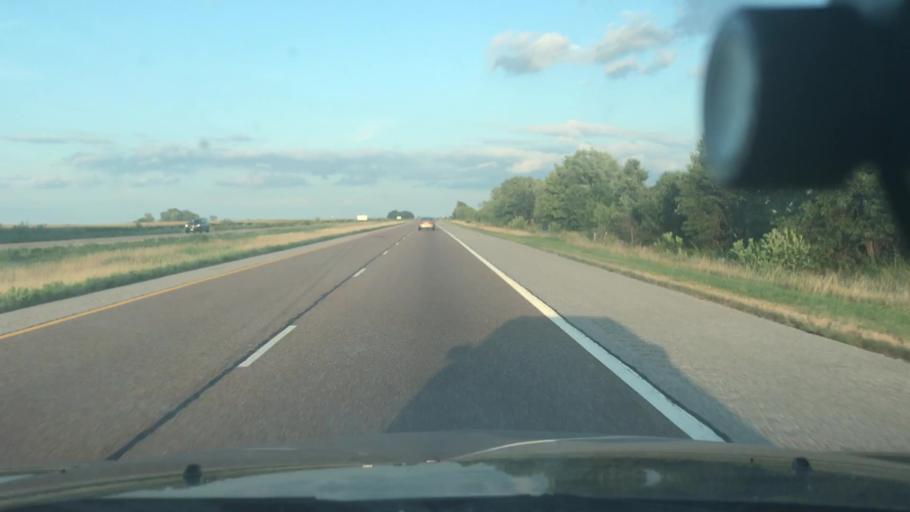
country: US
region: Illinois
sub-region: Clinton County
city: New Baden
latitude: 38.5451
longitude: -89.7483
